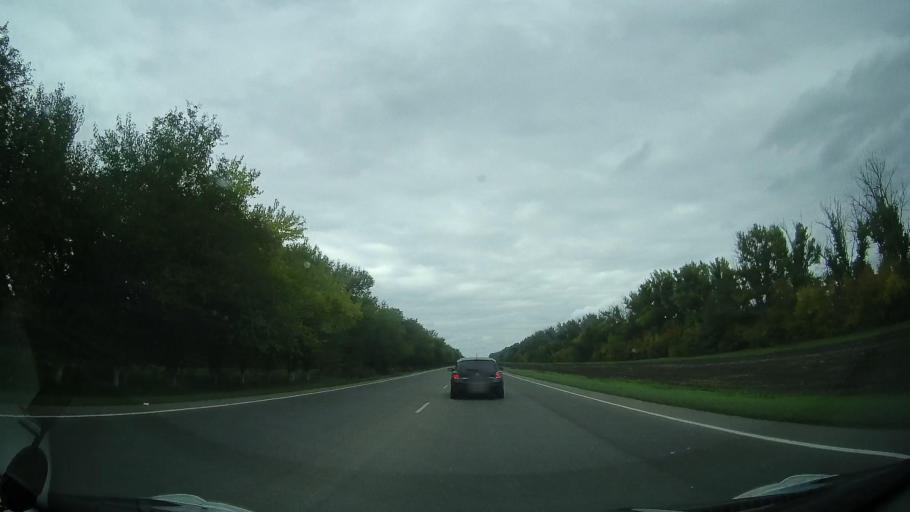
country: RU
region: Rostov
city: Yegorlykskaya
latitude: 46.6065
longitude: 40.6120
